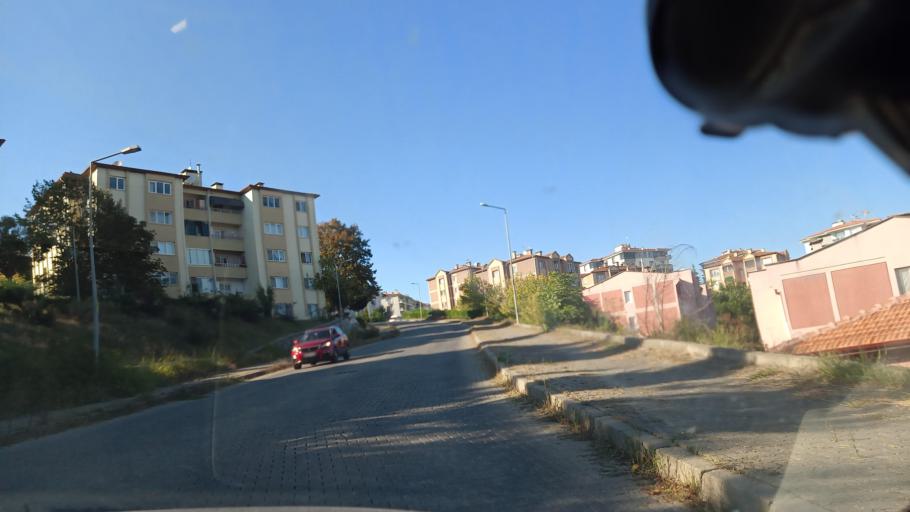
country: TR
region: Sakarya
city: Kazimpasa
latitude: 40.8587
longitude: 30.2925
